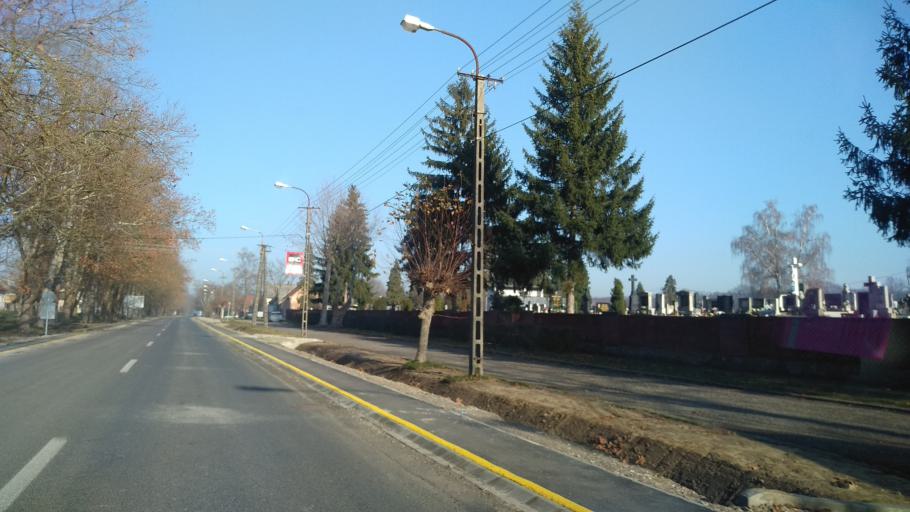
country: HU
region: Somogy
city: Barcs
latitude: 45.9681
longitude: 17.4589
